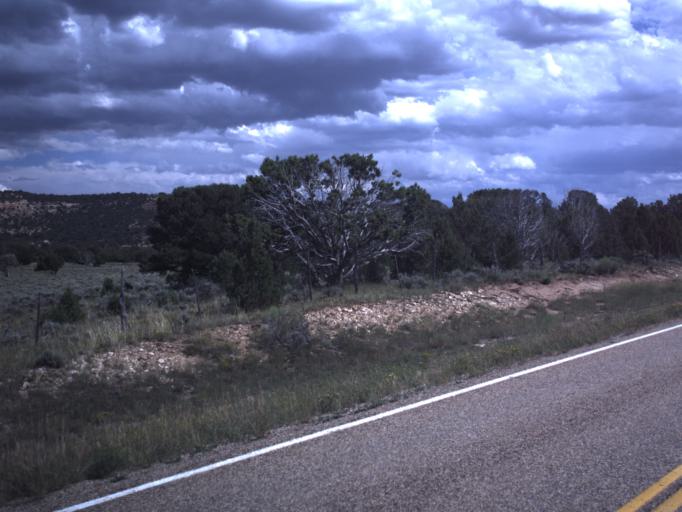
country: US
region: Utah
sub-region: Duchesne County
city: Duchesne
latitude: 40.3025
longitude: -110.6968
